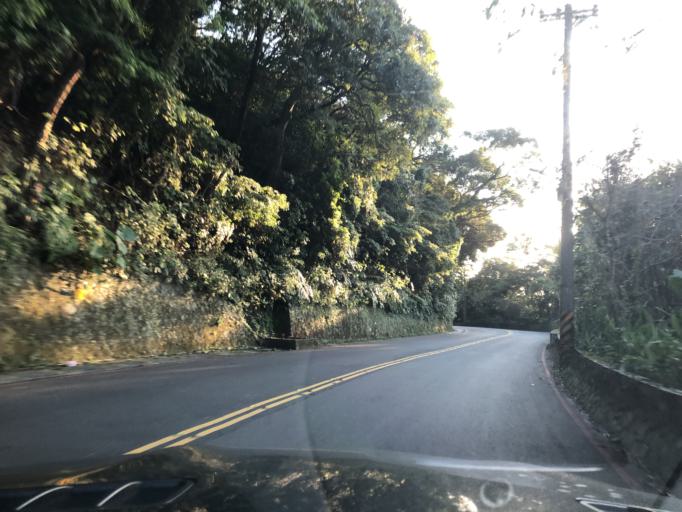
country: TW
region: Taipei
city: Taipei
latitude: 25.1413
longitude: 121.5529
